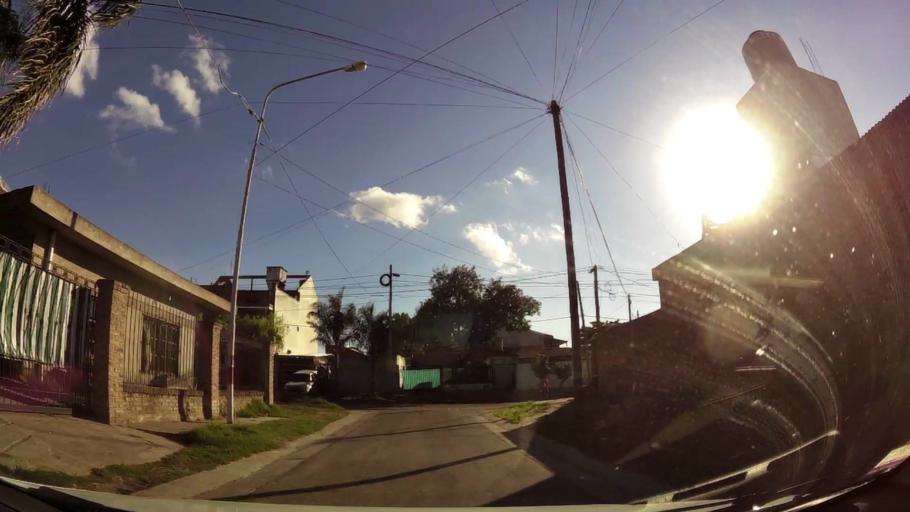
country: AR
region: Buenos Aires
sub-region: Partido de Moron
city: Moron
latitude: -34.6813
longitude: -58.6215
